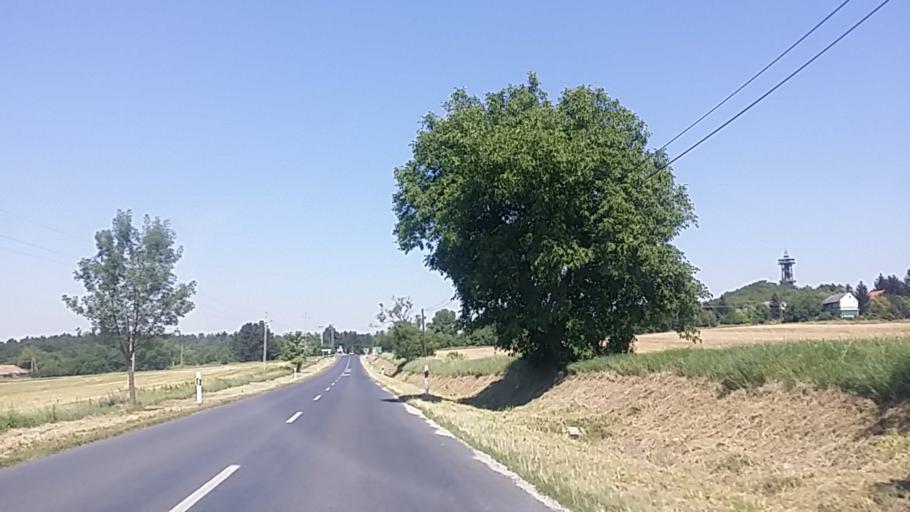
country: HU
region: Zala
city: Cserszegtomaj
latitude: 46.7952
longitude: 17.2088
